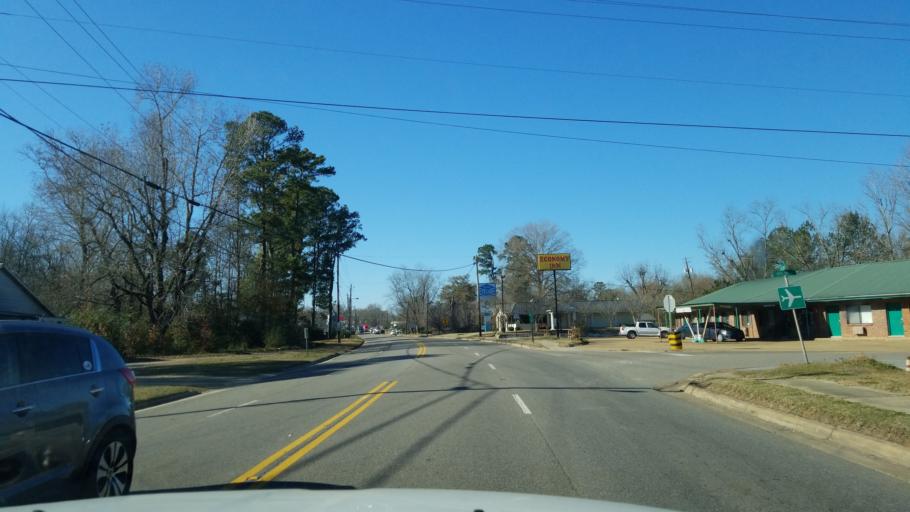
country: US
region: Alabama
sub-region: Pickens County
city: Reform
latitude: 33.3776
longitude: -88.0114
